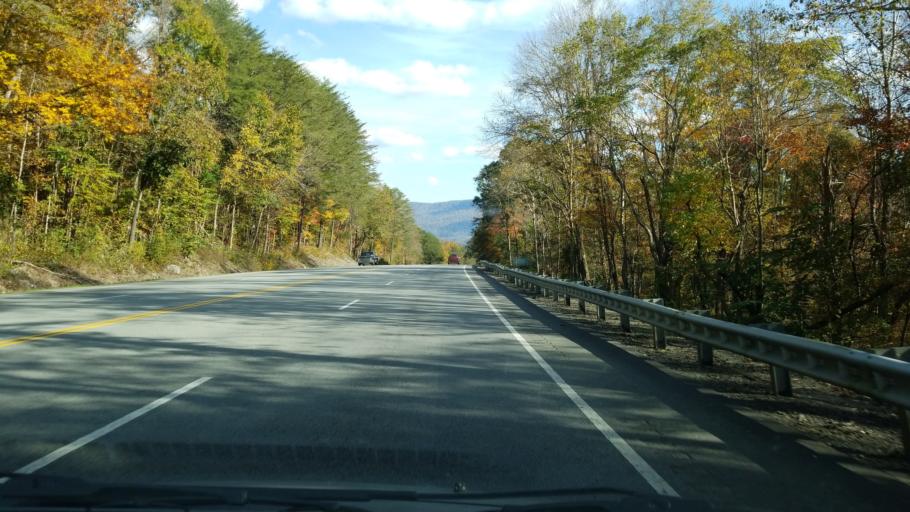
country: US
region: Tennessee
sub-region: Sequatchie County
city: Dunlap
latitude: 35.4062
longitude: -85.3967
